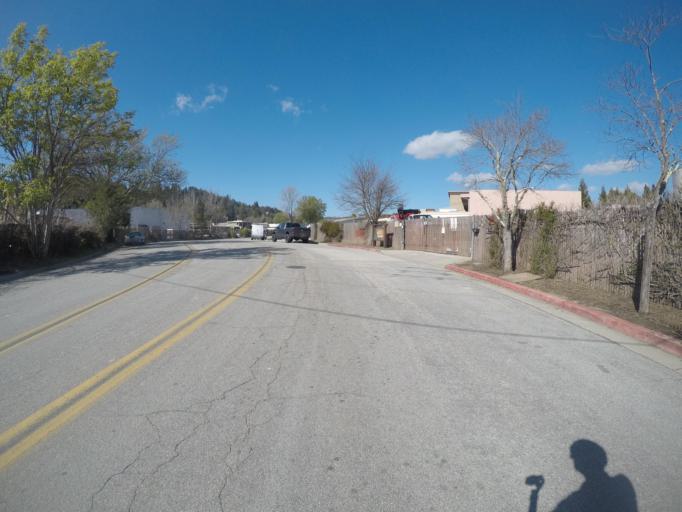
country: US
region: California
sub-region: Santa Cruz County
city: Scotts Valley
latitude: 37.0535
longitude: -122.0098
